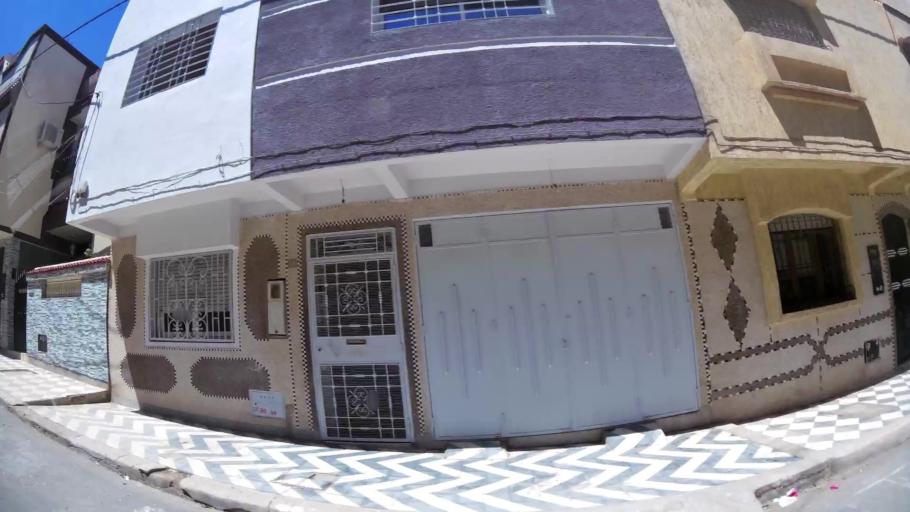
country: MA
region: Oriental
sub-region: Oujda-Angad
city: Oujda
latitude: 34.6672
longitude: -1.8863
